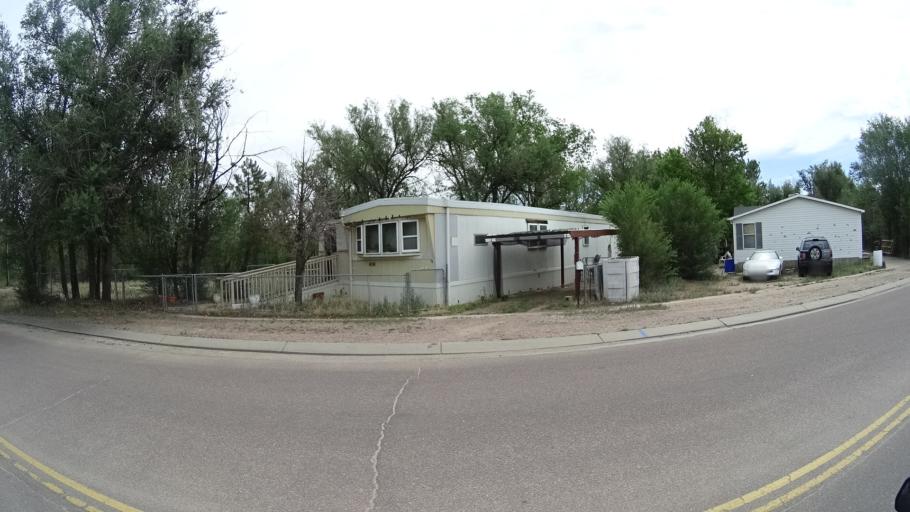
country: US
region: Colorado
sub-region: El Paso County
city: Fountain
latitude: 38.6785
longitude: -104.7075
